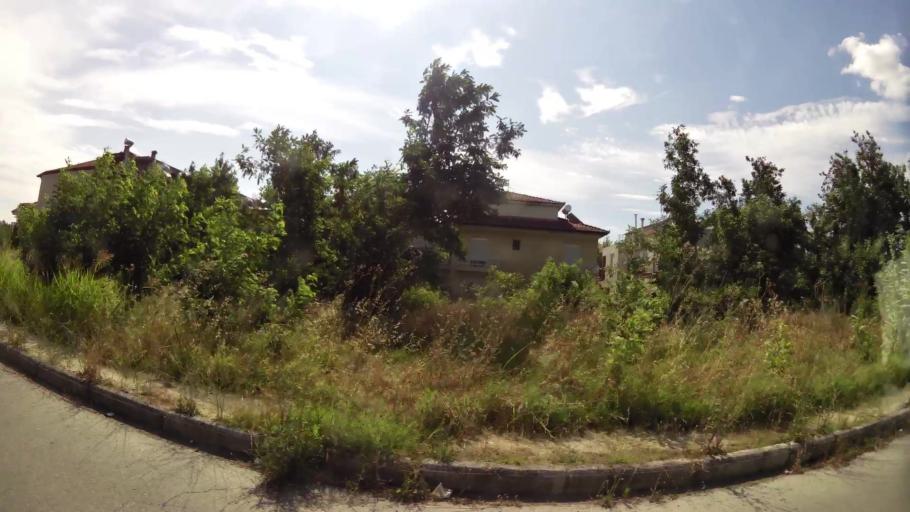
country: GR
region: Central Macedonia
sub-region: Nomos Pierias
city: Katerini
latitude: 40.2778
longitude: 22.4902
